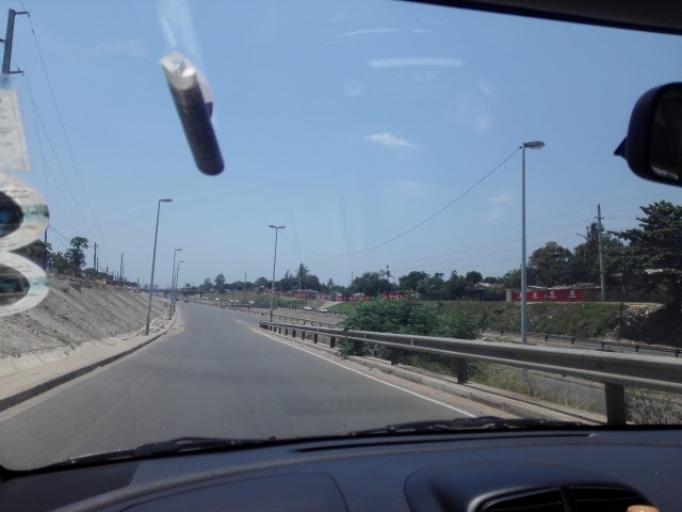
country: MZ
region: Maputo City
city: Maputo
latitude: -25.9296
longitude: 32.5579
